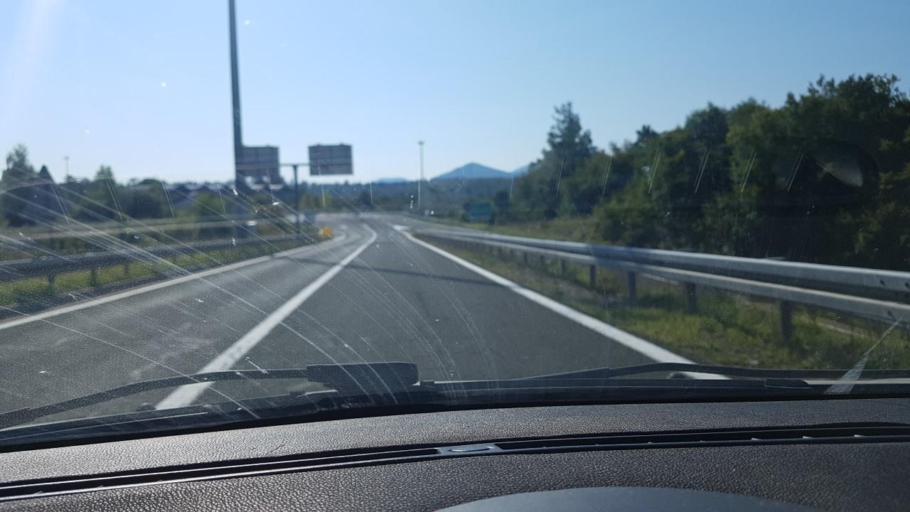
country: HR
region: Primorsko-Goranska
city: Vrbovsko
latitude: 45.3636
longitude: 15.0845
